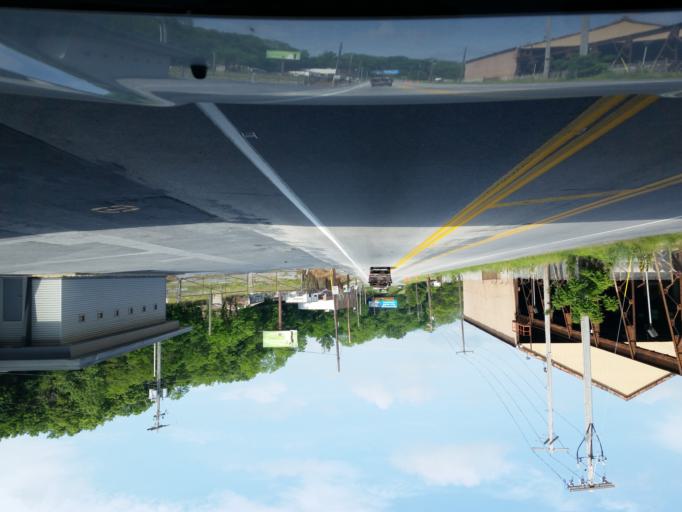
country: US
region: Pennsylvania
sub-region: Dauphin County
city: Highspire
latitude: 40.2123
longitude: -76.7978
